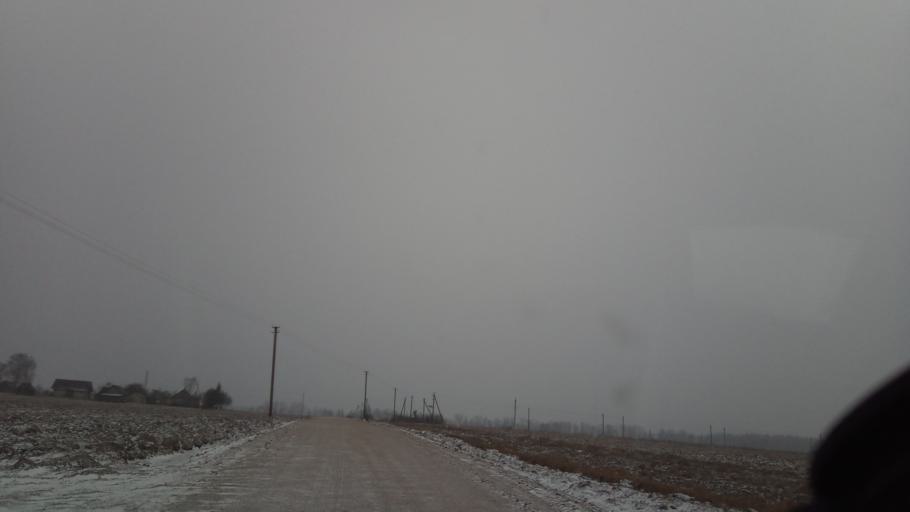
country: LT
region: Vilnius County
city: Ukmerge
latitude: 55.3443
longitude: 24.9570
